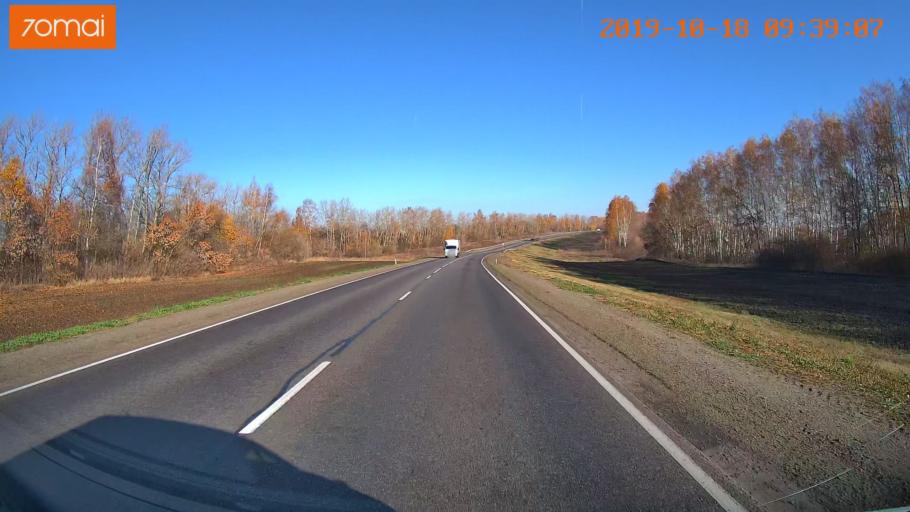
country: RU
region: Tula
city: Yefremov
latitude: 53.2484
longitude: 38.1343
